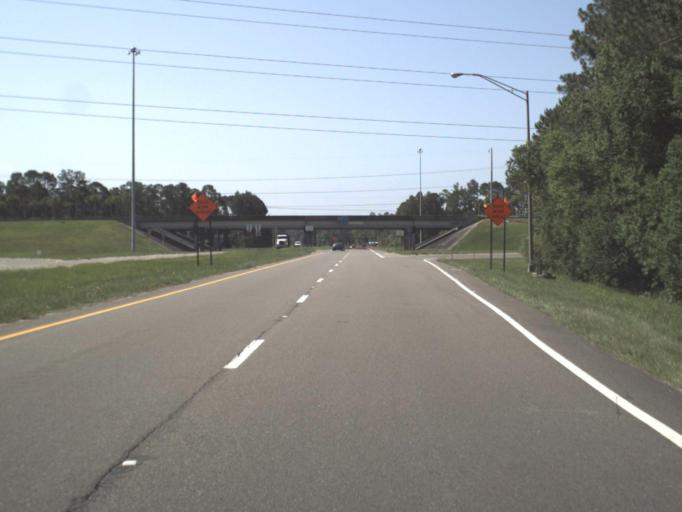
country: US
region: Florida
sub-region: Nassau County
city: Nassau Village-Ratliff
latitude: 30.4570
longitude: -81.7064
